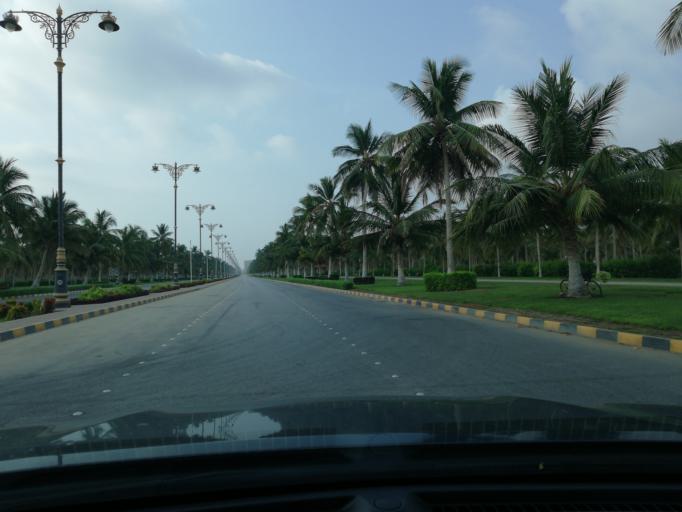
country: OM
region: Zufar
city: Salalah
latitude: 17.0375
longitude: 54.1069
